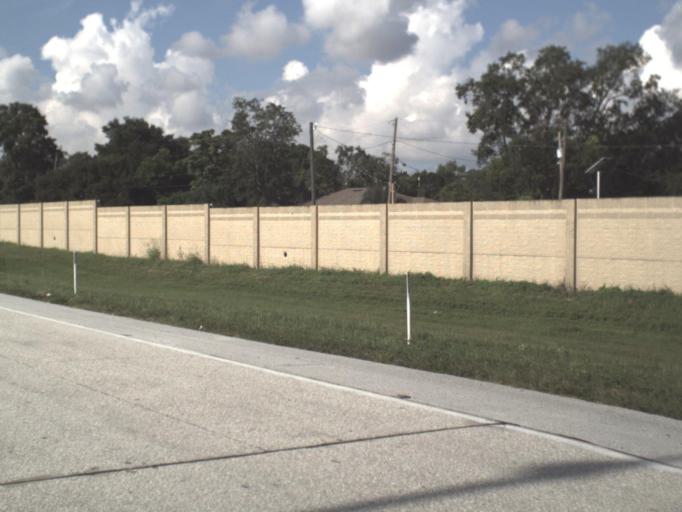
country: US
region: Florida
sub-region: Hillsborough County
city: University
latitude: 28.0588
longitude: -82.4548
